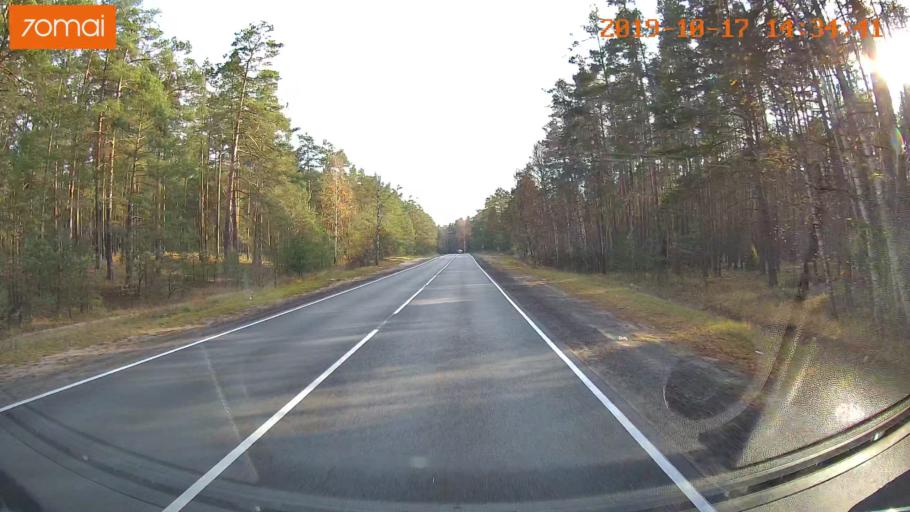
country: RU
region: Rjazan
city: Solotcha
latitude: 54.9090
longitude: 39.9986
